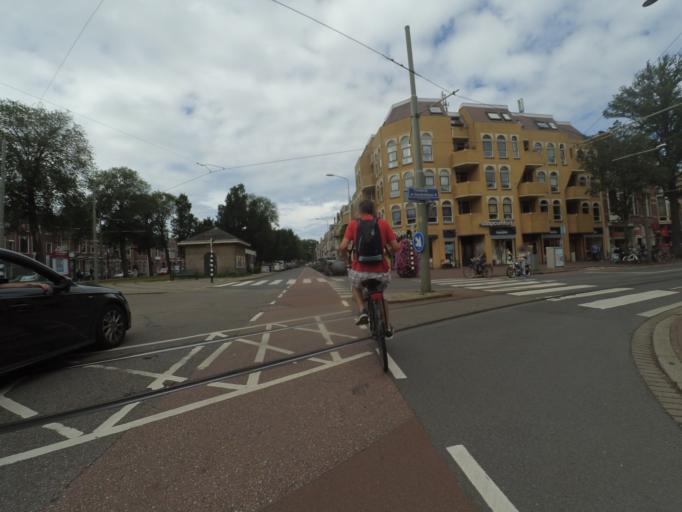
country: NL
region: South Holland
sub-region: Gemeente Den Haag
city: Scheveningen
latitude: 52.0929
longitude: 4.2762
